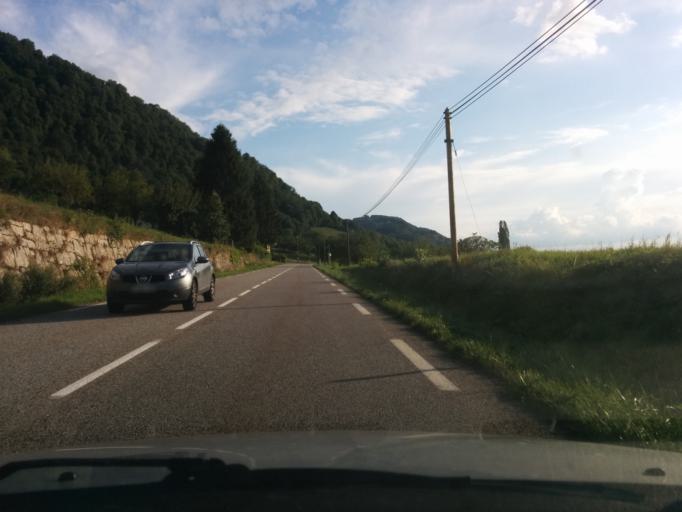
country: FR
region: Rhone-Alpes
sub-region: Departement de la Savoie
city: Saint-Beron
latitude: 45.4960
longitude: 5.7288
